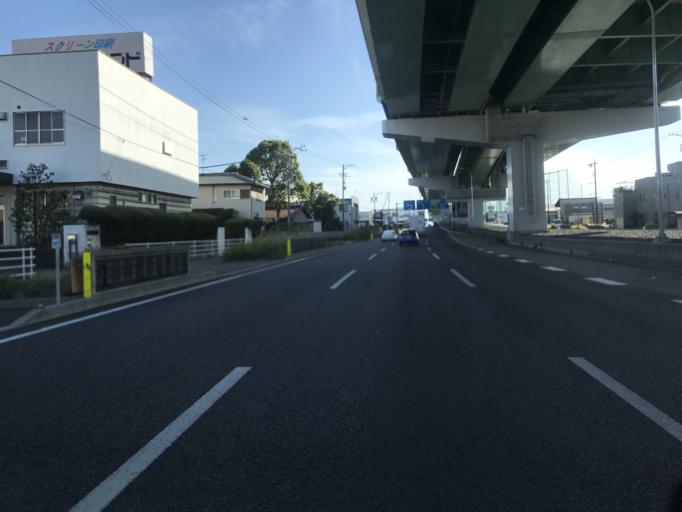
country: JP
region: Aichi
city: Iwakura
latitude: 35.2611
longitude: 136.8418
